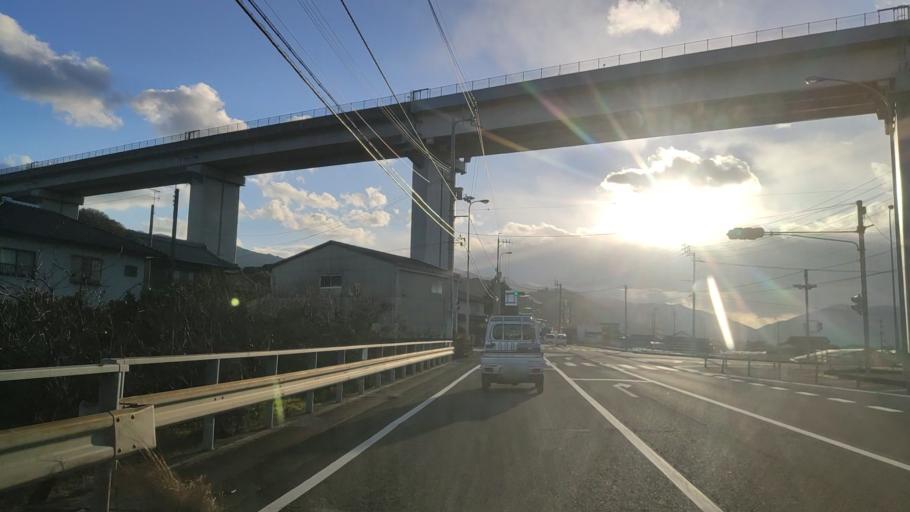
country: JP
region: Ehime
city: Saijo
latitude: 33.8895
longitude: 133.0867
